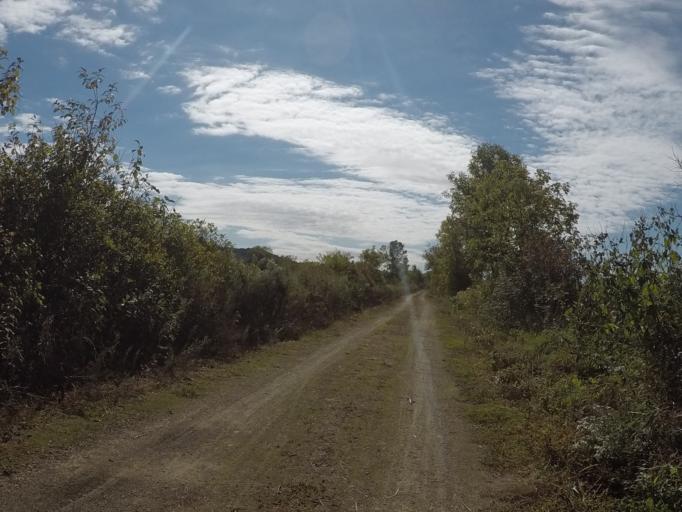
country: US
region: Wisconsin
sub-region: Richland County
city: Richland Center
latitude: 43.2728
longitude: -90.3105
